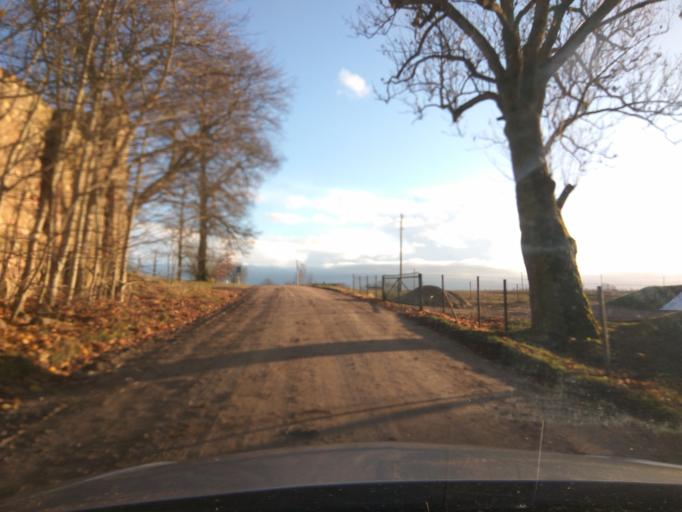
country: LV
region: Aizpute
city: Aizpute
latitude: 56.7668
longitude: 21.7098
